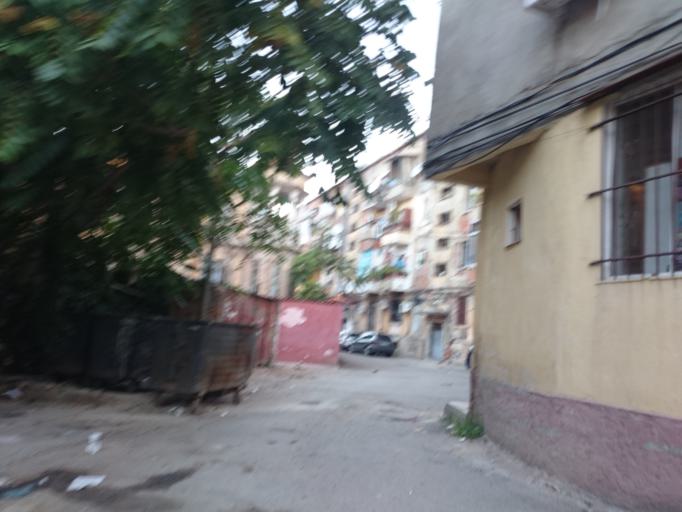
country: AL
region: Tirane
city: Tirana
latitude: 41.3311
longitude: 19.8088
